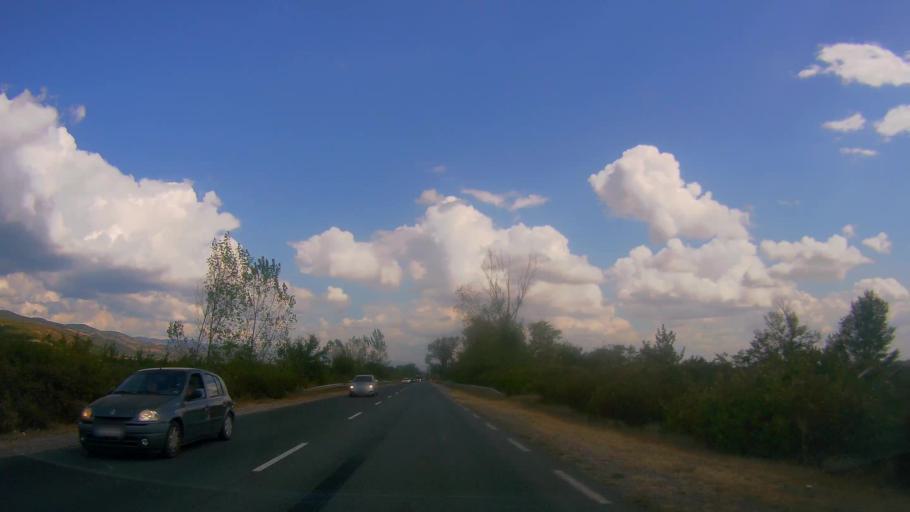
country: BG
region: Sliven
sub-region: Obshtina Sliven
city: Sliven
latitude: 42.6341
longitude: 26.2083
